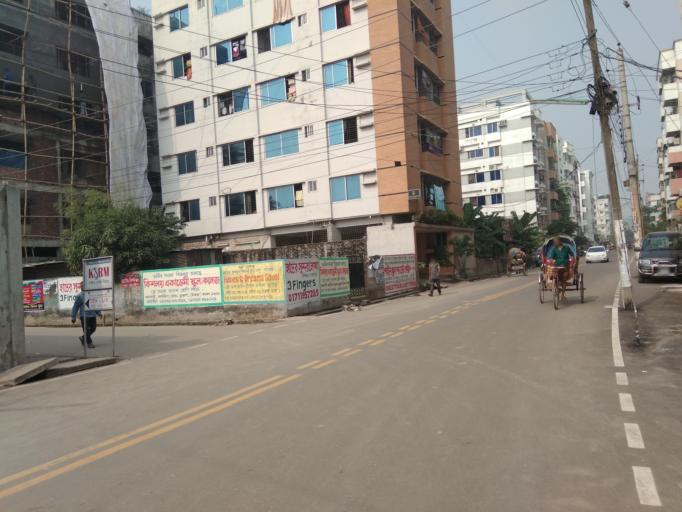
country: BD
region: Dhaka
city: Tungi
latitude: 23.8671
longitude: 90.3834
